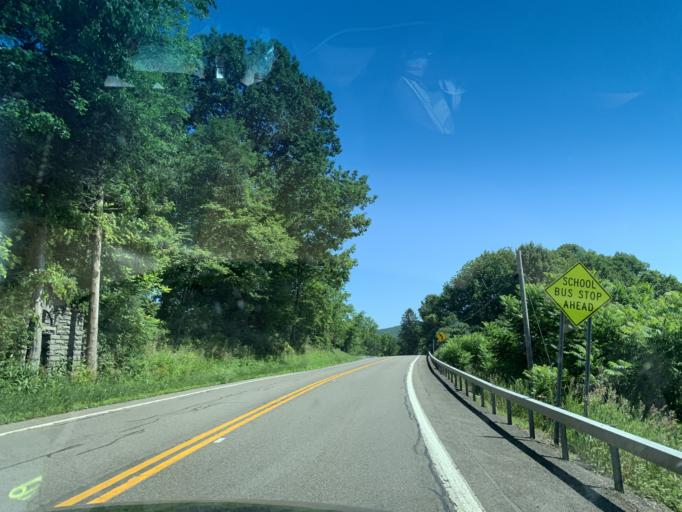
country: US
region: New York
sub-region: Chenango County
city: Norwich
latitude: 42.4833
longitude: -75.4053
